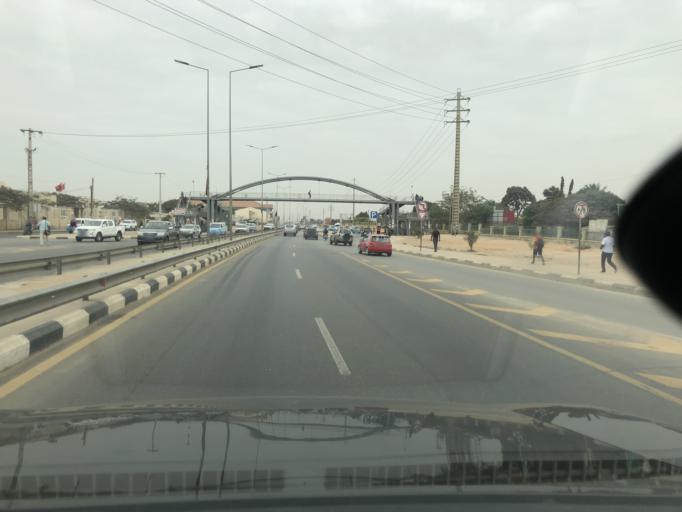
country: AO
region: Luanda
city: Luanda
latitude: -8.8997
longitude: 13.2609
